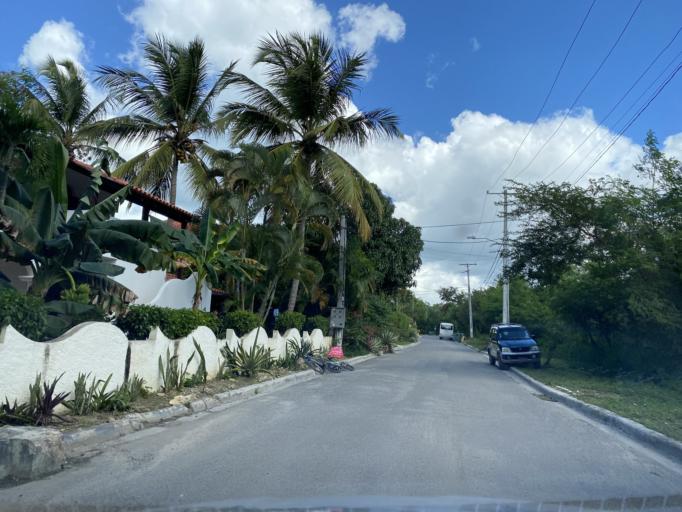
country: DO
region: La Romana
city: La Romana
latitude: 18.3471
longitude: -68.8255
